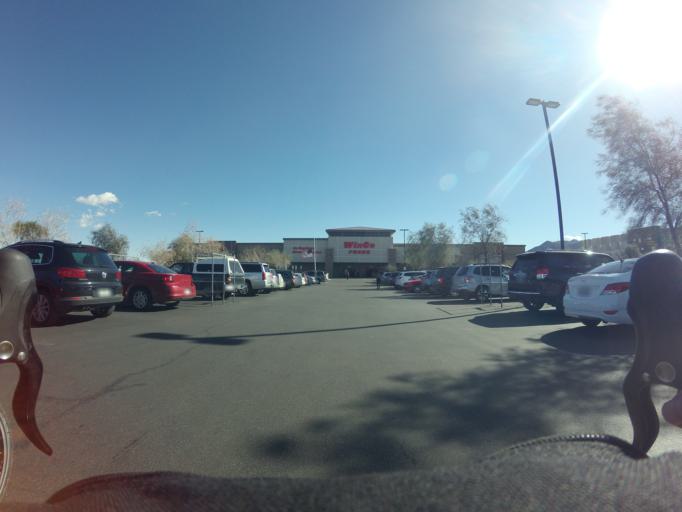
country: US
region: Nevada
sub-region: Clark County
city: Whitney
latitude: 36.0336
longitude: -115.0450
